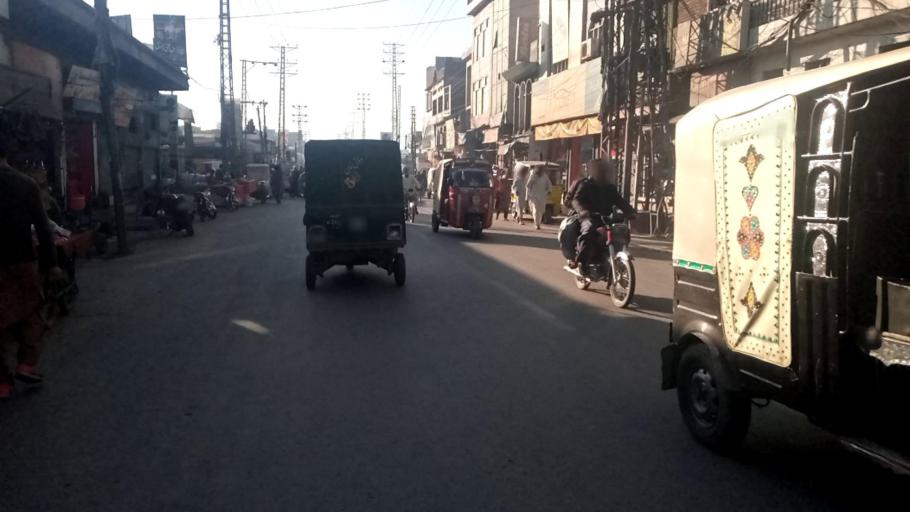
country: PK
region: Khyber Pakhtunkhwa
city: Mingora
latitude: 34.7723
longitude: 72.3540
